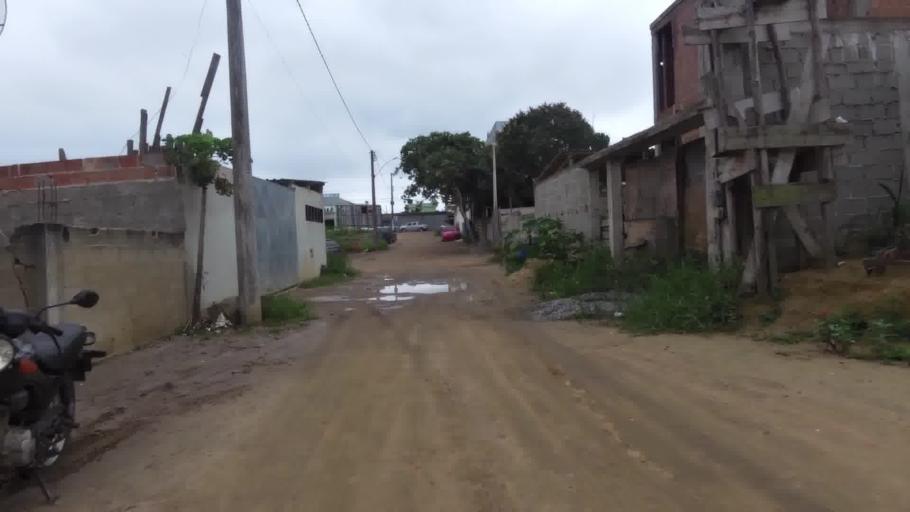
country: BR
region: Espirito Santo
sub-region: Marataizes
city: Marataizes
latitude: -21.0468
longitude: -40.8403
